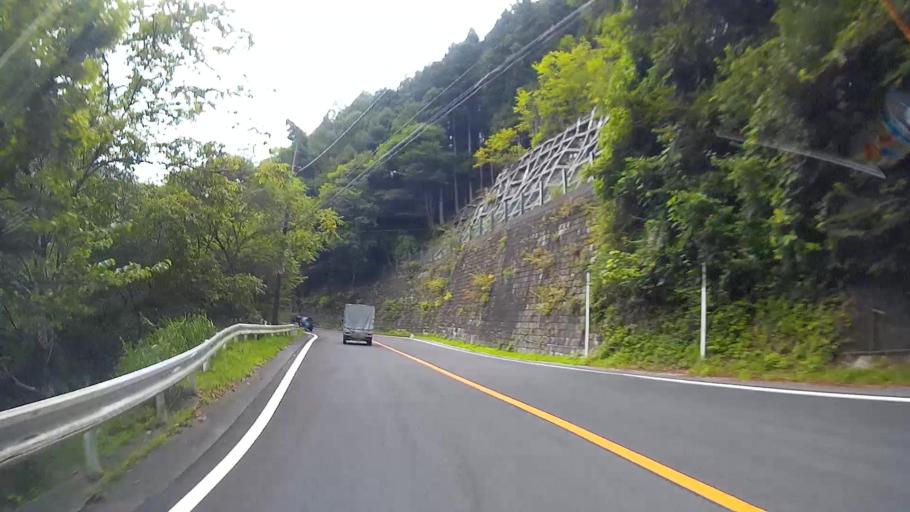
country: JP
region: Saitama
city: Chichibu
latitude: 35.9302
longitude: 138.8344
